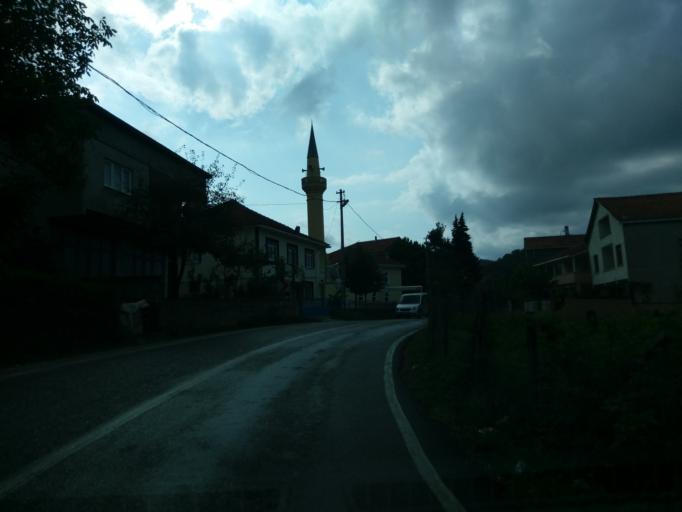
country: TR
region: Sinop
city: Helaldi
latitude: 41.9363
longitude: 34.4086
